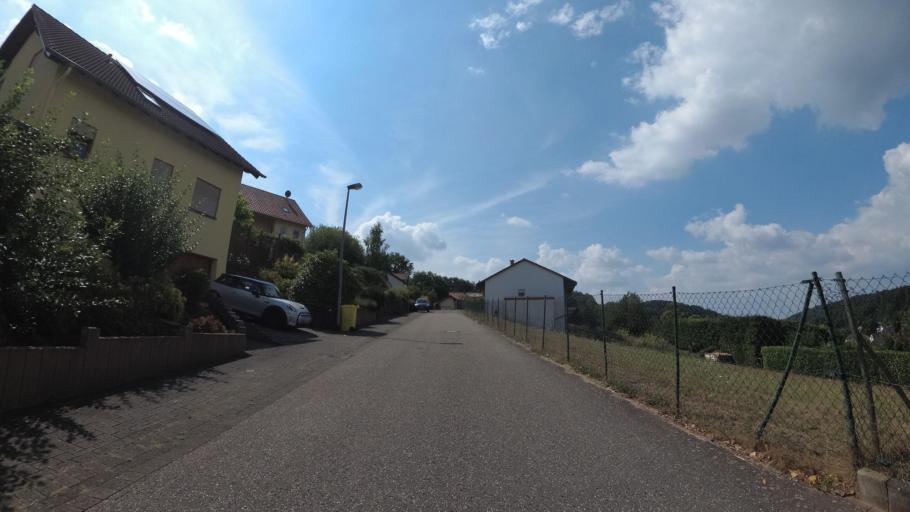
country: DE
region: Rheinland-Pfalz
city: Contwig
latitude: 49.2721
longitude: 7.4232
